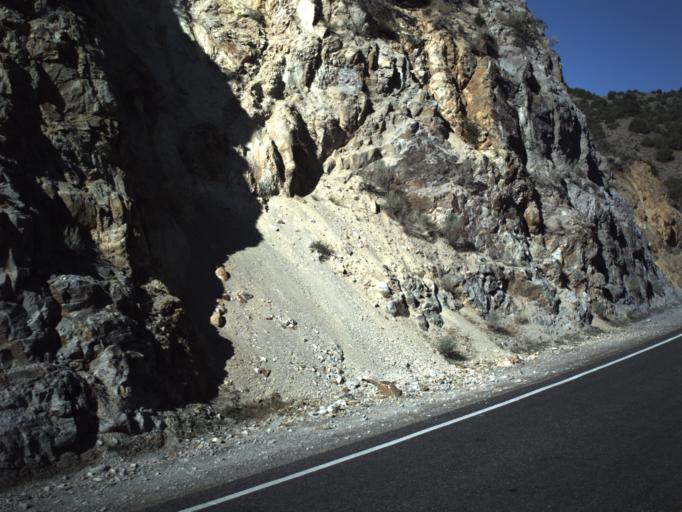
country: US
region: Utah
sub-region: Utah County
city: Genola
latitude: 39.9726
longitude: -112.0659
